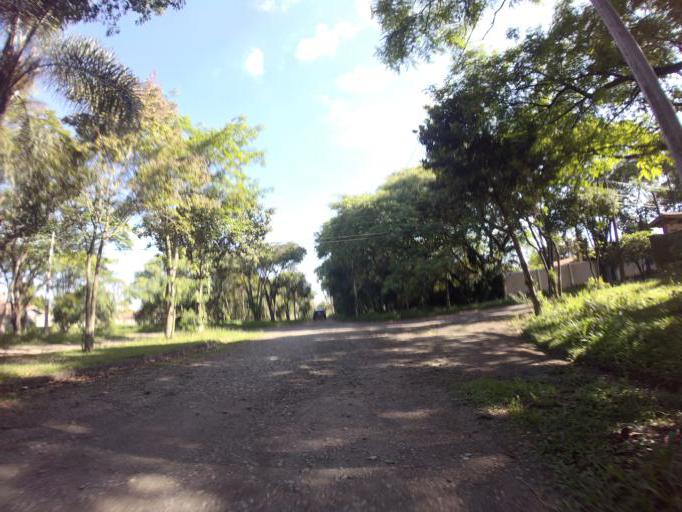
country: BR
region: Sao Paulo
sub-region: Piracicaba
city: Piracicaba
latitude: -22.7509
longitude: -47.5840
